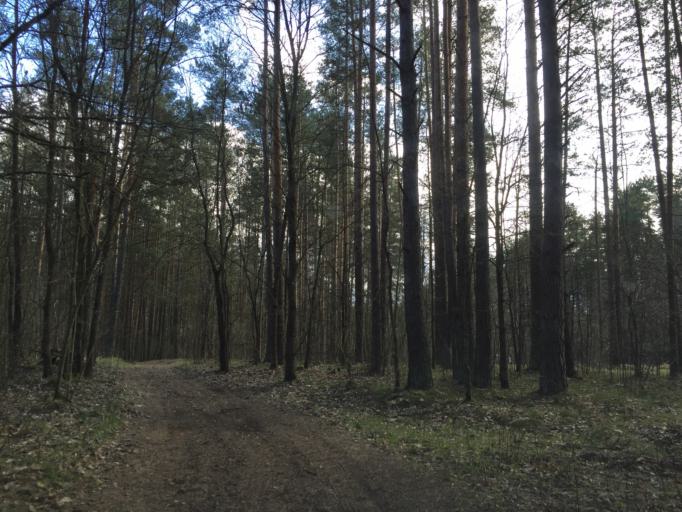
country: LV
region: Riga
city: Bergi
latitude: 57.0018
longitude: 24.2922
